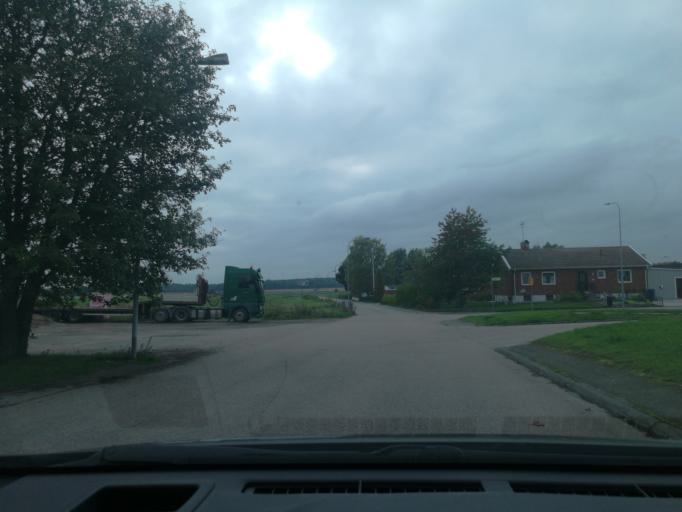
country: SE
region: Vaestmanland
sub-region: Vasteras
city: Tillberga
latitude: 59.6835
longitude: 16.6205
